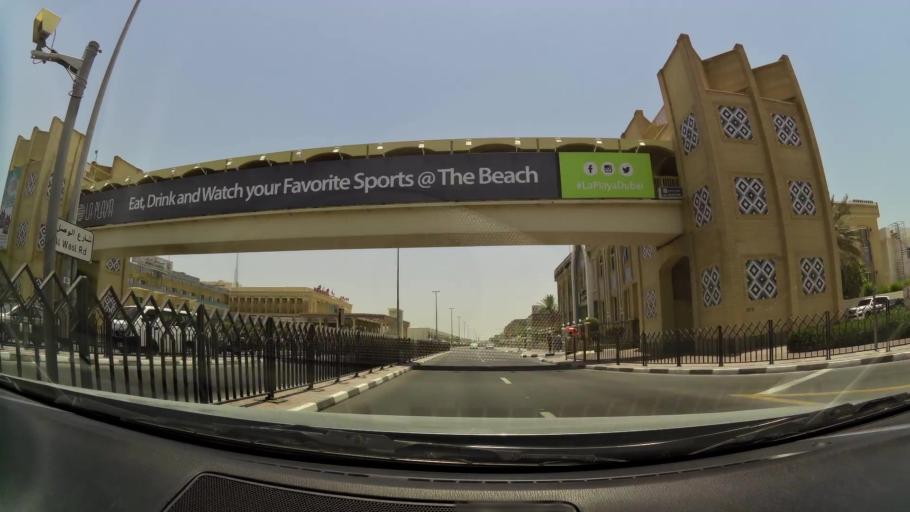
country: AE
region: Ash Shariqah
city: Sharjah
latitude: 25.2314
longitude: 55.2688
